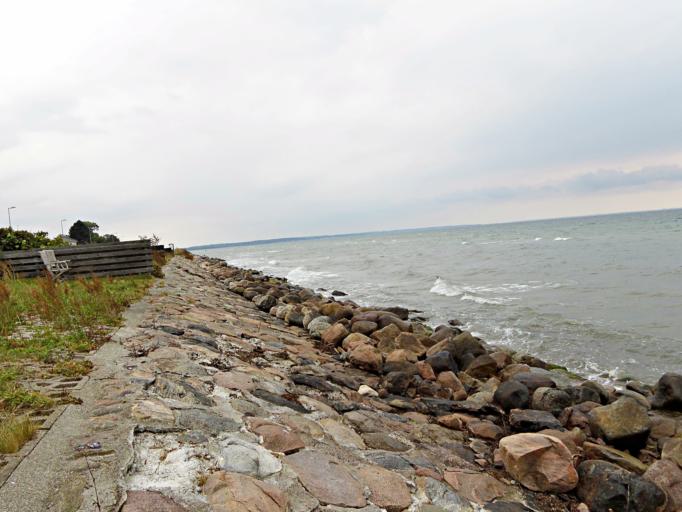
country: DK
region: Capital Region
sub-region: Horsholm Kommune
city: Horsholm
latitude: 55.8955
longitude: 12.5369
